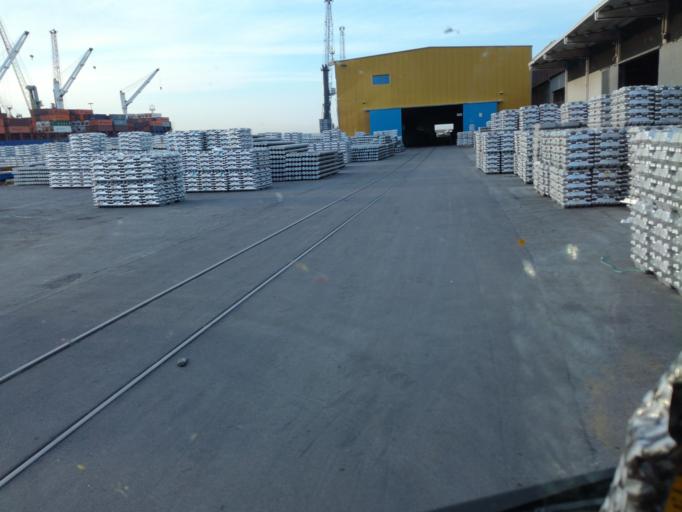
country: IT
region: Liguria
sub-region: Provincia di Genova
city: San Teodoro
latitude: 44.4061
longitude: 8.8936
